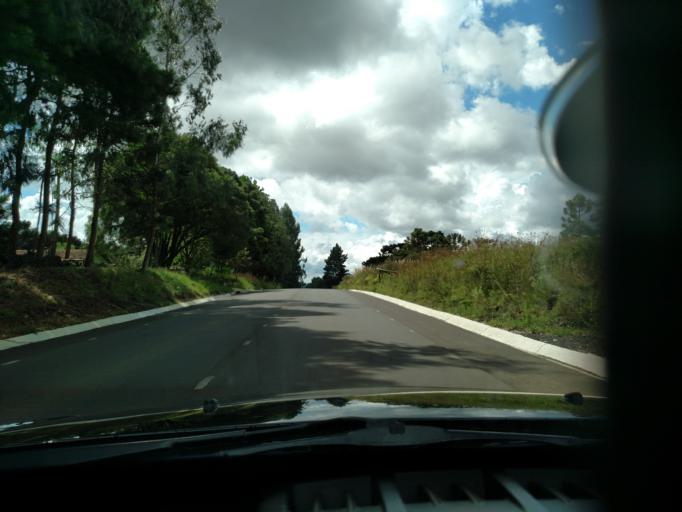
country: BR
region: Santa Catarina
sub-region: Lages
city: Lages
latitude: -27.9505
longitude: -50.0954
